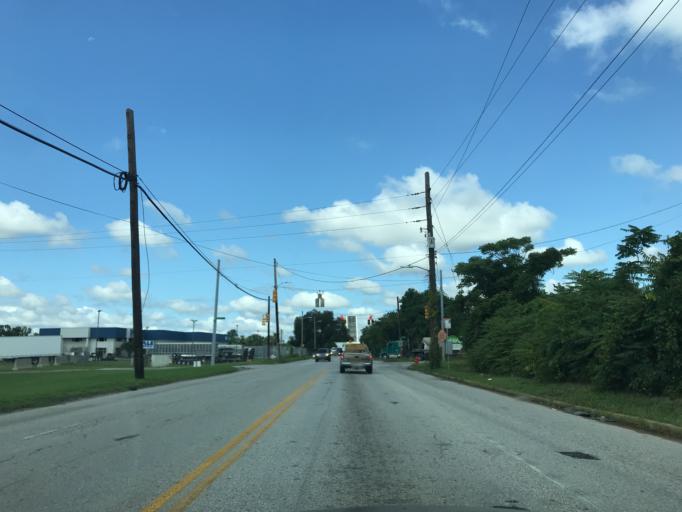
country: US
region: Maryland
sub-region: Anne Arundel County
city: Brooklyn Park
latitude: 39.2058
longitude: -76.5726
